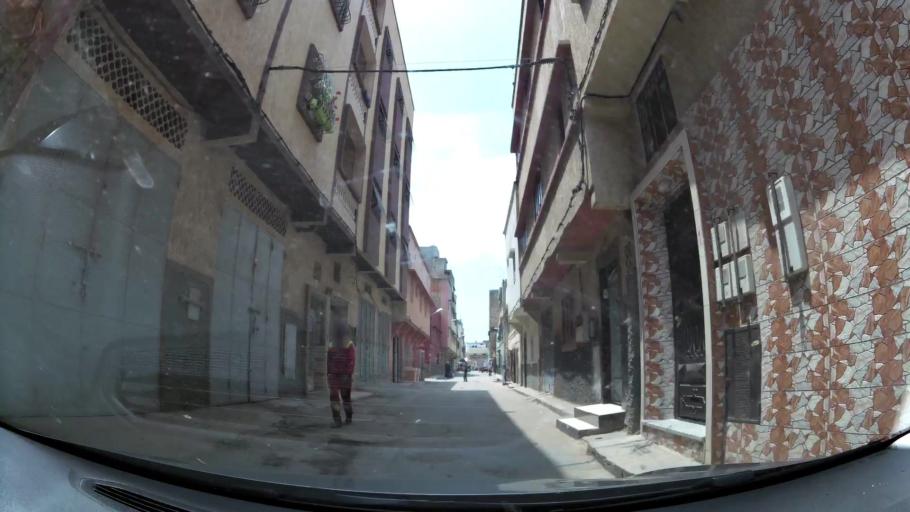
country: MA
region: Rabat-Sale-Zemmour-Zaer
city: Sale
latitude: 34.0536
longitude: -6.7874
